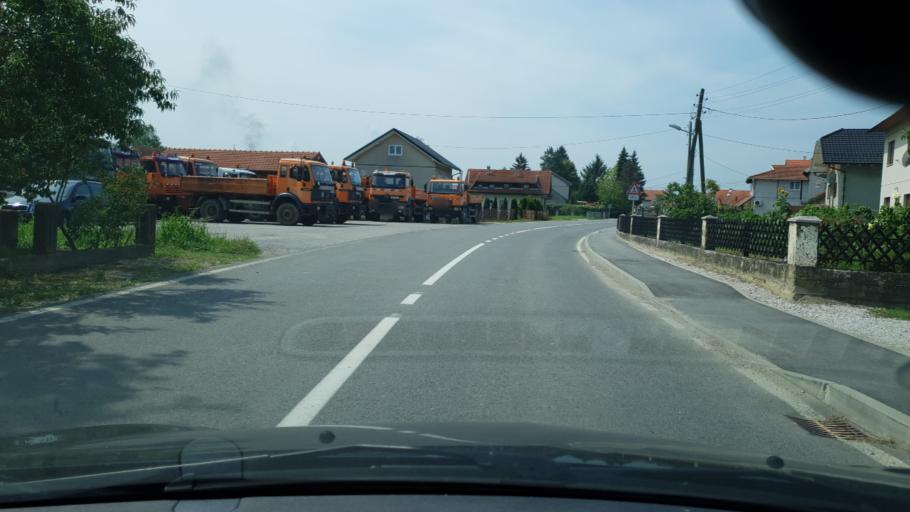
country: HR
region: Krapinsko-Zagorska
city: Bedekovcina
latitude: 46.0267
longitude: 15.9612
